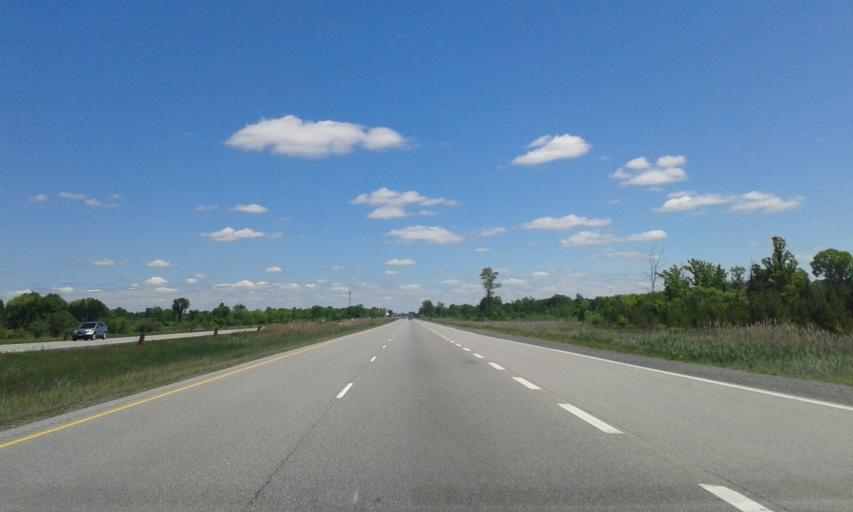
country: US
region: New York
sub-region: St. Lawrence County
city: Norfolk
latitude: 44.9541
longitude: -75.1074
